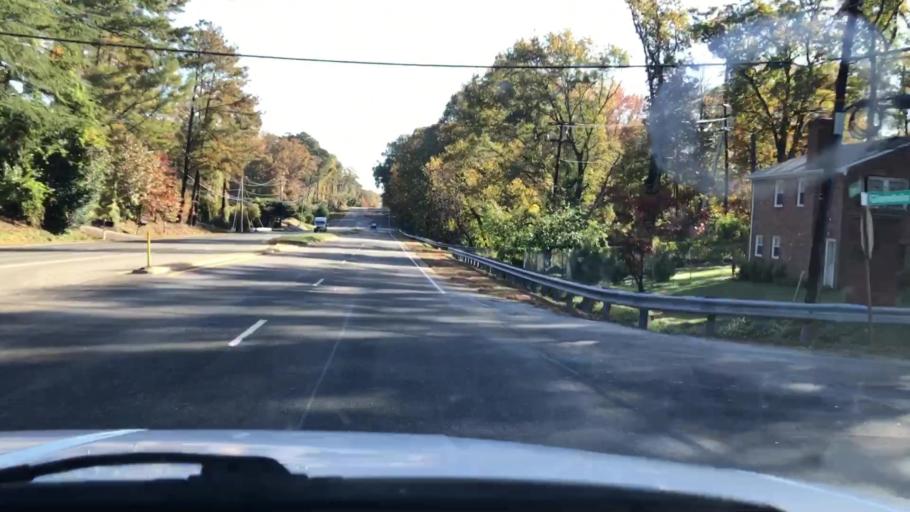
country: US
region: Virginia
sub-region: Henrico County
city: Tuckahoe
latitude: 37.5942
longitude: -77.5589
